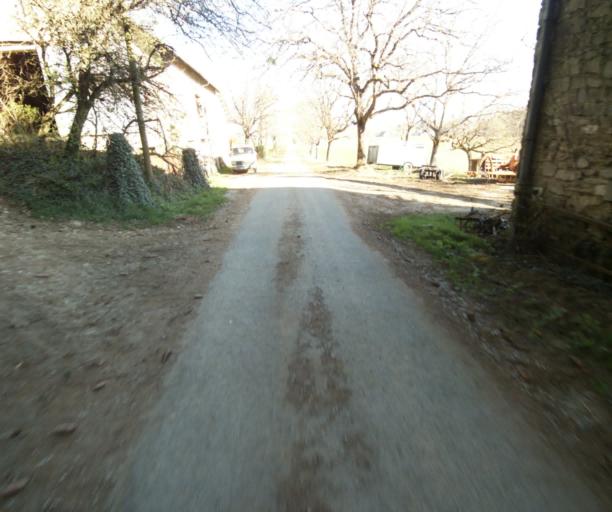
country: FR
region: Limousin
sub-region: Departement de la Correze
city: Uzerche
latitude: 45.3879
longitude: 1.6204
